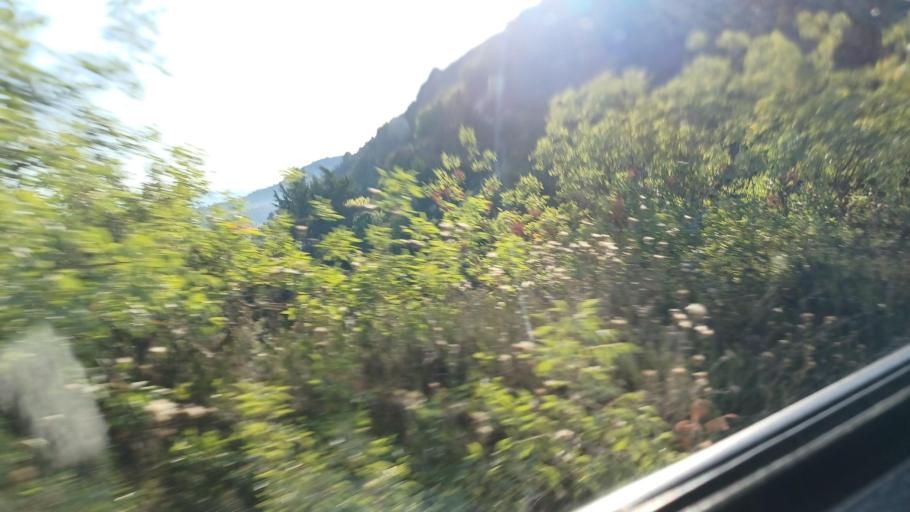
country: CY
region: Pafos
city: Tala
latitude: 34.8676
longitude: 32.4615
